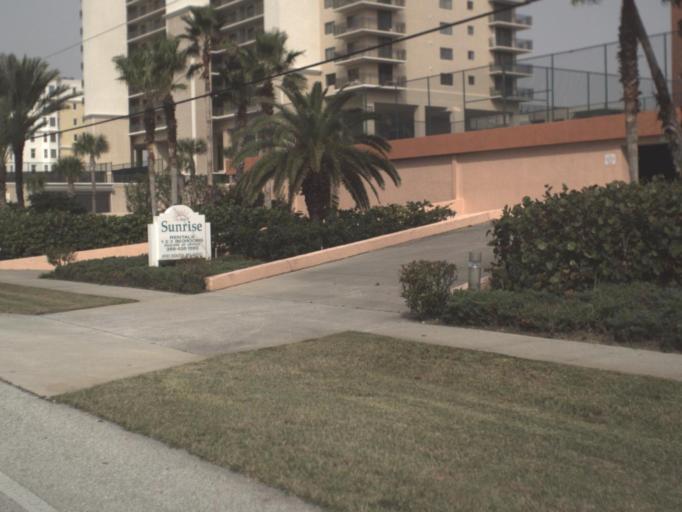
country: US
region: Florida
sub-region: Volusia County
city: Edgewater
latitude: 29.0048
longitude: -80.8766
